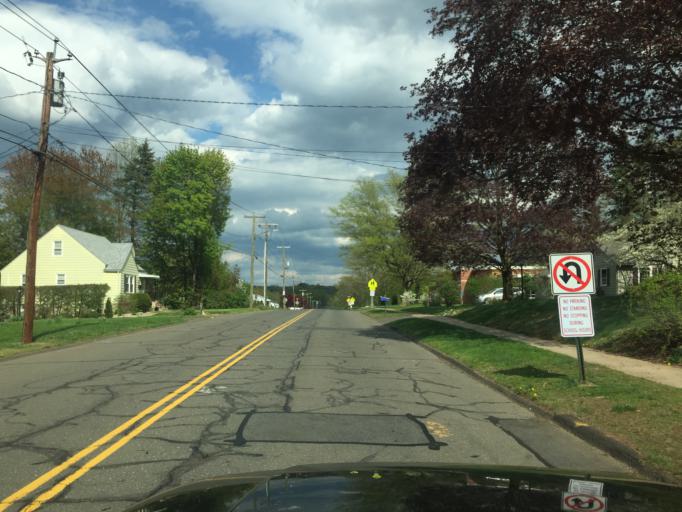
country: US
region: Connecticut
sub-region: Hartford County
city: Kensington
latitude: 41.6224
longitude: -72.7549
